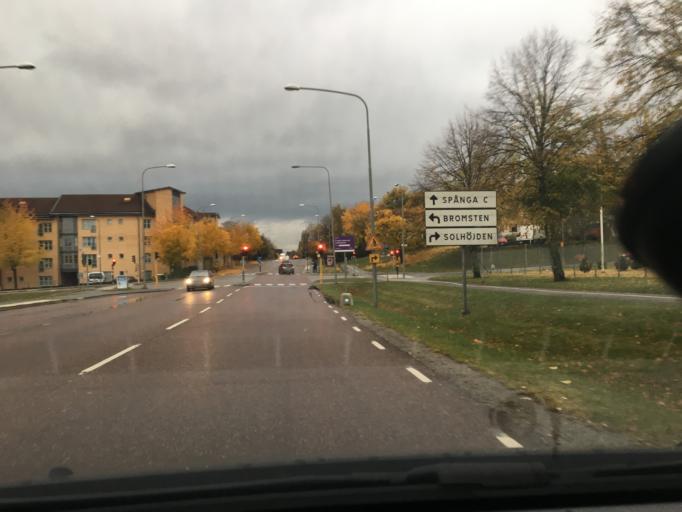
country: SE
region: Stockholm
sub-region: Stockholms Kommun
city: Kista
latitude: 59.3861
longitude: 17.9072
